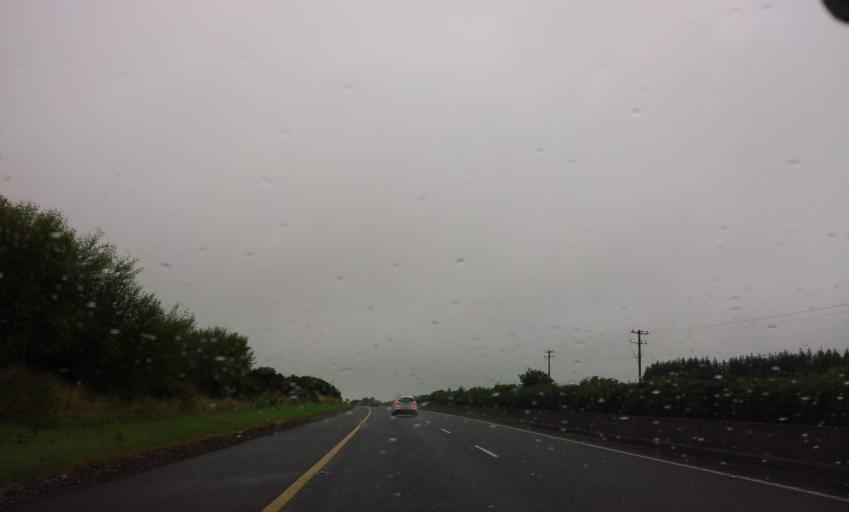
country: IE
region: Munster
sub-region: County Cork
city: Mitchelstown
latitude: 52.2086
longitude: -8.2754
